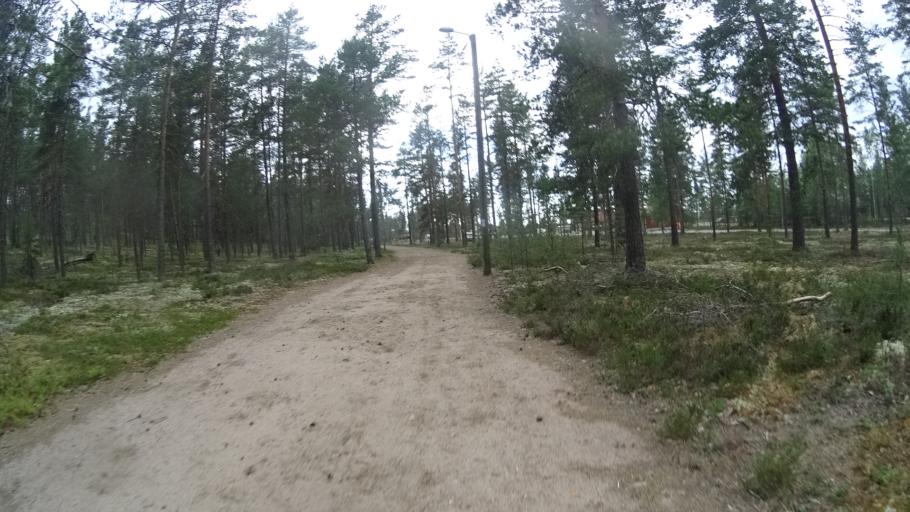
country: FI
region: Satakunta
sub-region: Pohjois-Satakunta
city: Jaemijaervi
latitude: 61.7766
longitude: 22.7275
